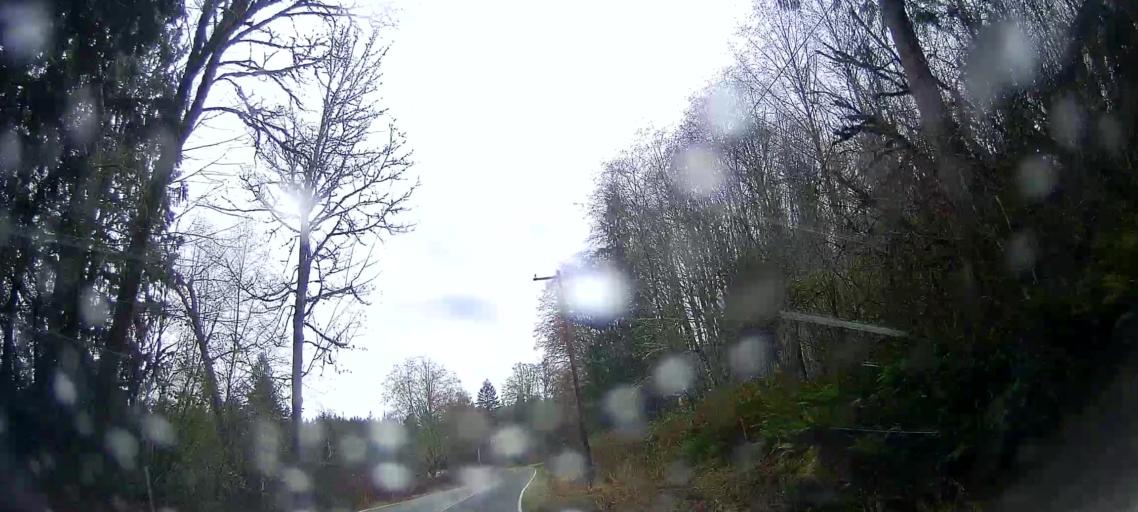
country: US
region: Washington
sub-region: Skagit County
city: Clear Lake
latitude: 48.4692
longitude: -122.1712
